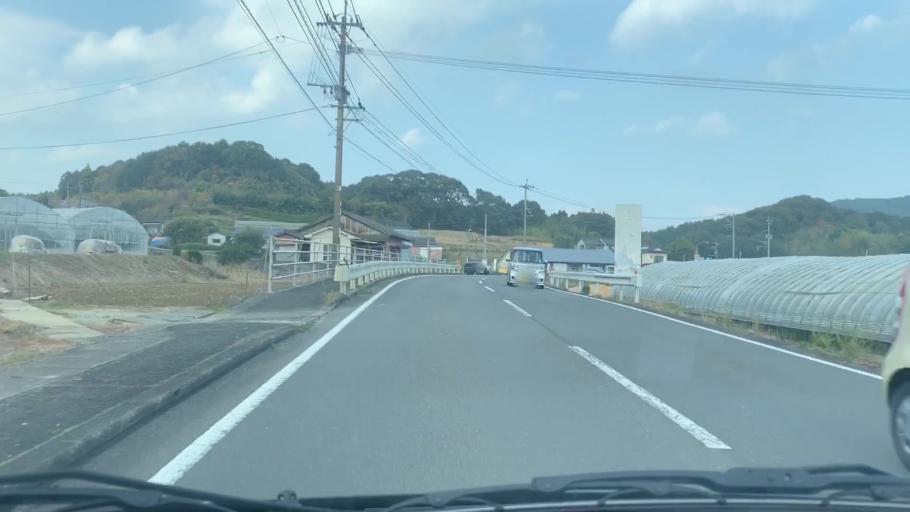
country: JP
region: Nagasaki
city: Togitsu
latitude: 32.9677
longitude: 129.7809
